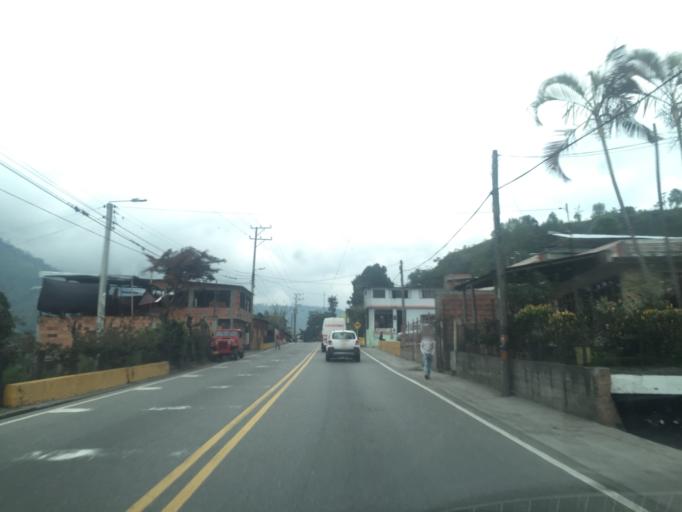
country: CO
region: Tolima
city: Cajamarca
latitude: 4.4367
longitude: -75.4374
